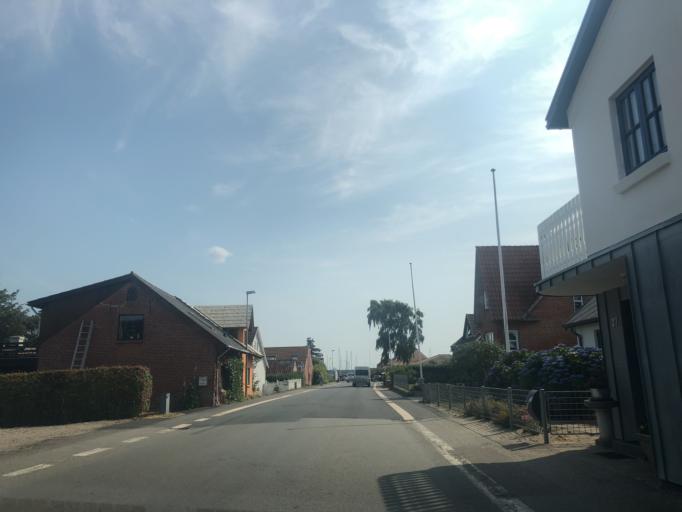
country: DK
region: North Denmark
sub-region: Morso Kommune
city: Nykobing Mors
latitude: 56.8060
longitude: 9.0202
